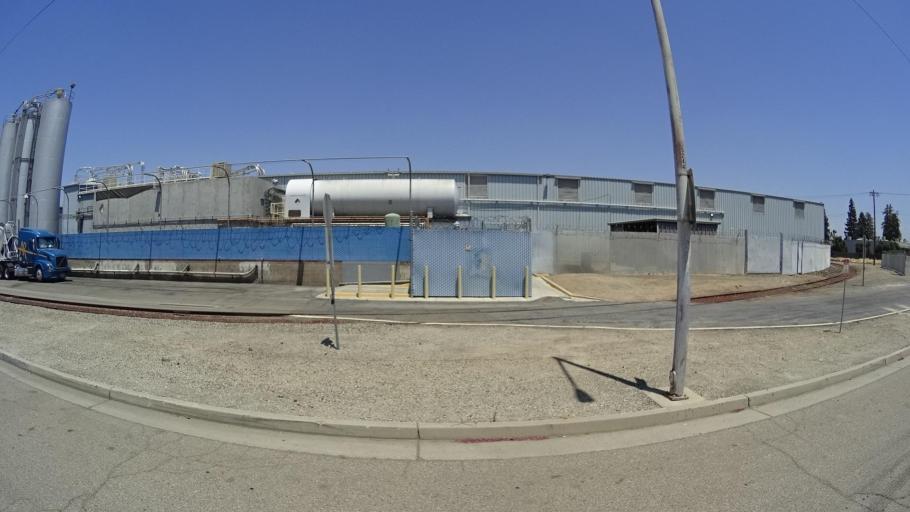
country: US
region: California
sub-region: Fresno County
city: Sunnyside
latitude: 36.7618
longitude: -119.7102
